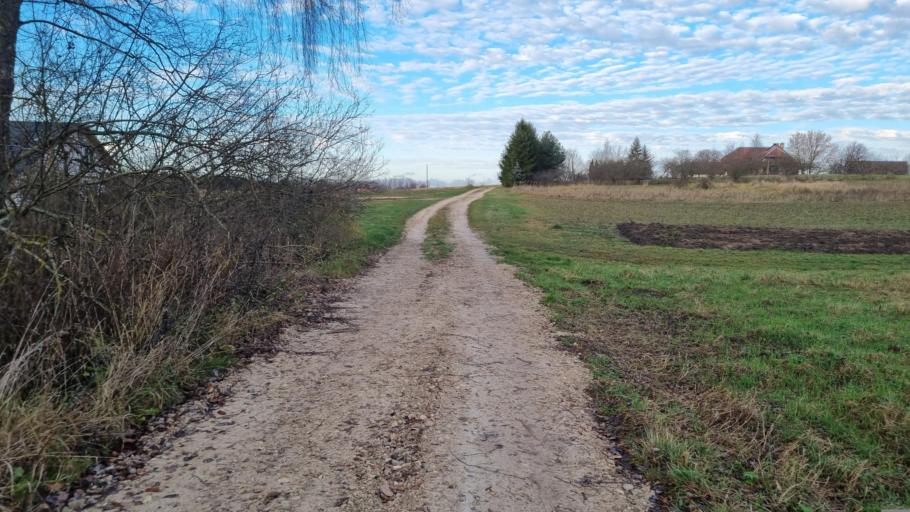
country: LV
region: Kekava
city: Kekava
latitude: 56.7853
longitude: 24.2482
